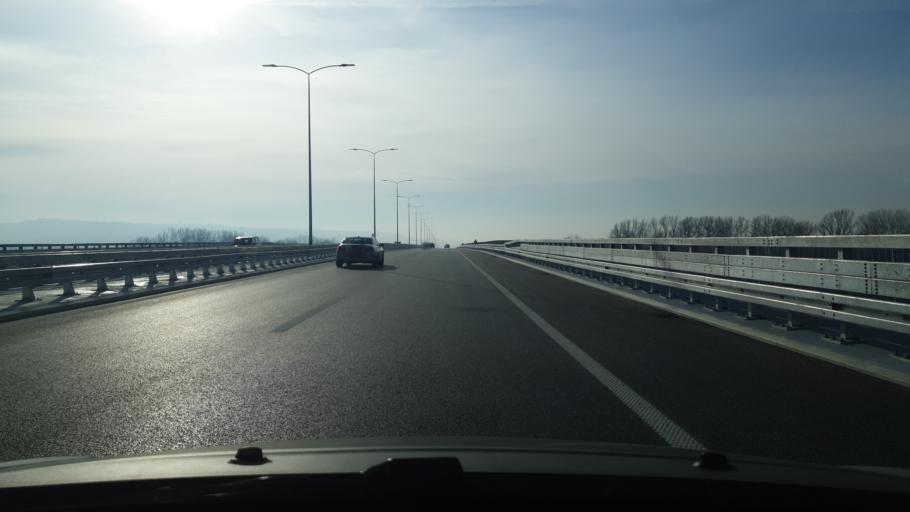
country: RS
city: Baric
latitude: 44.6661
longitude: 20.2461
